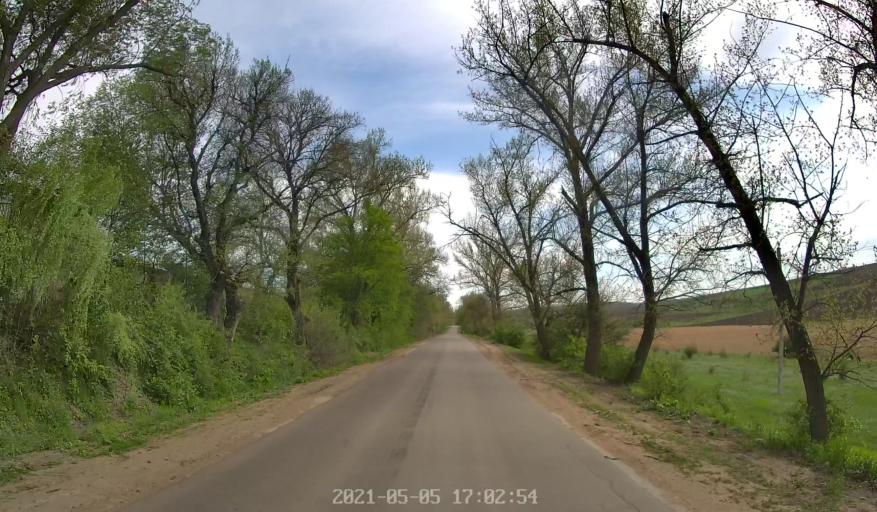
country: MD
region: Chisinau
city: Vadul lui Voda
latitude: 47.0563
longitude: 29.1324
